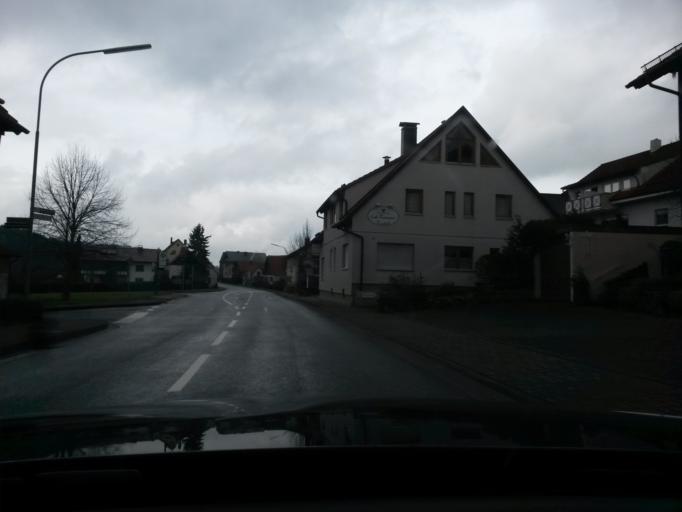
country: DE
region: Hesse
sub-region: Regierungsbezirk Kassel
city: Hilders
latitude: 50.5547
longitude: 10.0102
